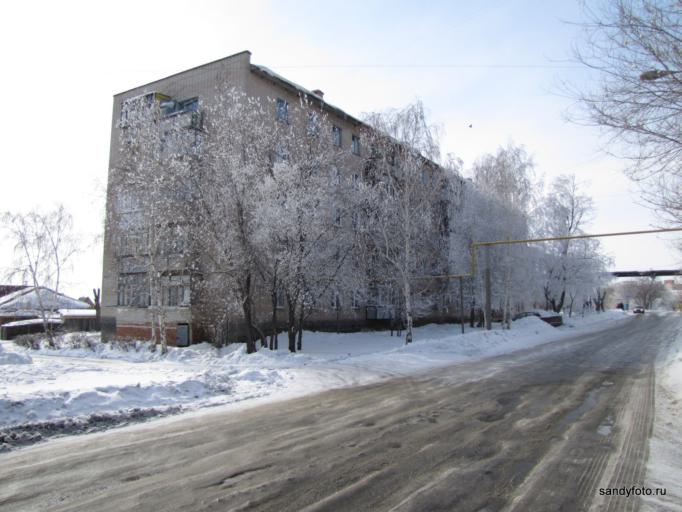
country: RU
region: Chelyabinsk
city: Troitsk
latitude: 54.1033
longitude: 61.5595
